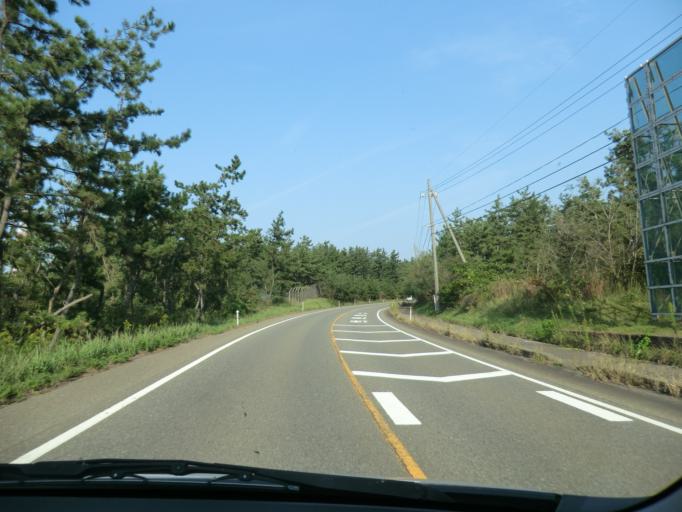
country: JP
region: Niigata
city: Kashiwazaki
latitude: 37.4177
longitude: 138.5876
